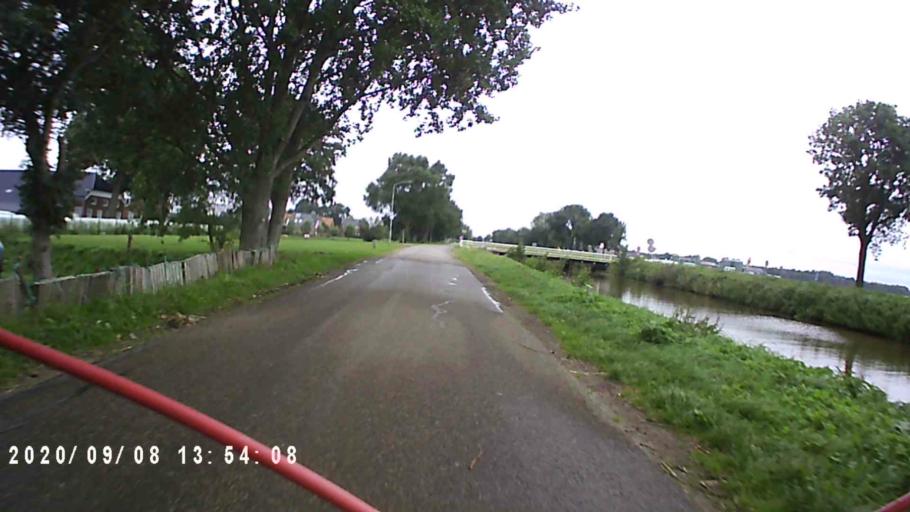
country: NL
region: Groningen
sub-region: Gemeente Veendam
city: Veendam
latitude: 53.1517
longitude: 6.8641
